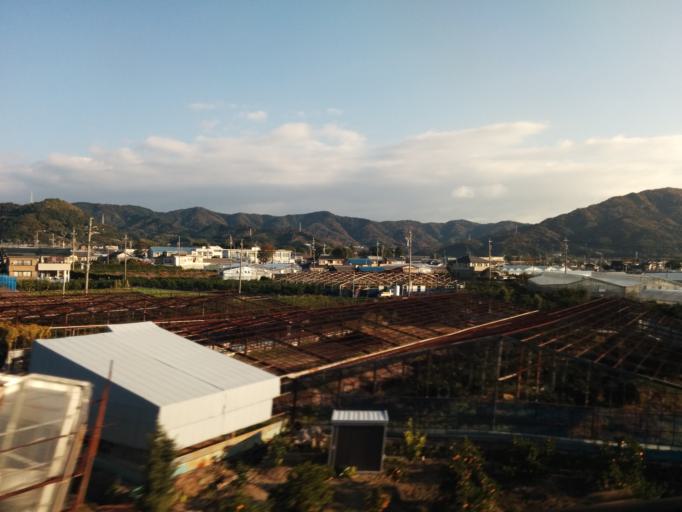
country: JP
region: Aichi
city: Gamagori
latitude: 34.8365
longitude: 137.2215
